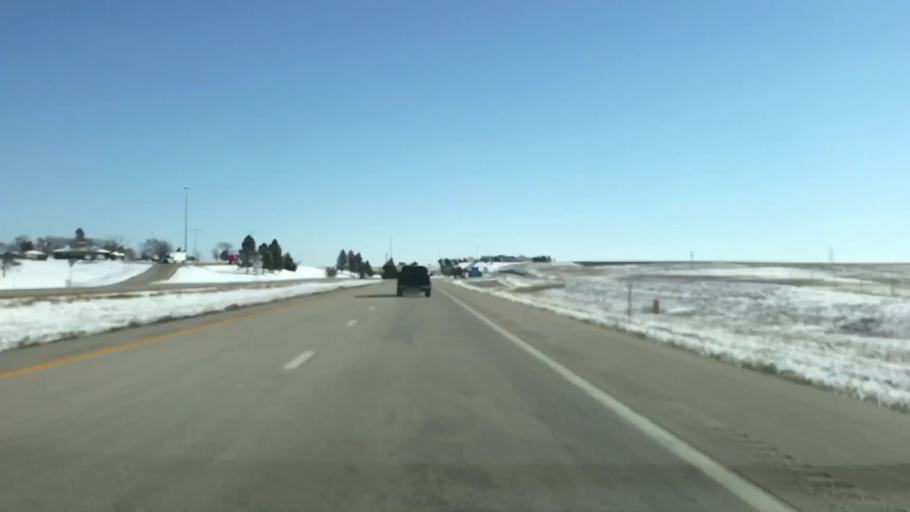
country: US
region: Kansas
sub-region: Sherman County
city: Goodland
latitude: 39.3291
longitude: -101.9205
